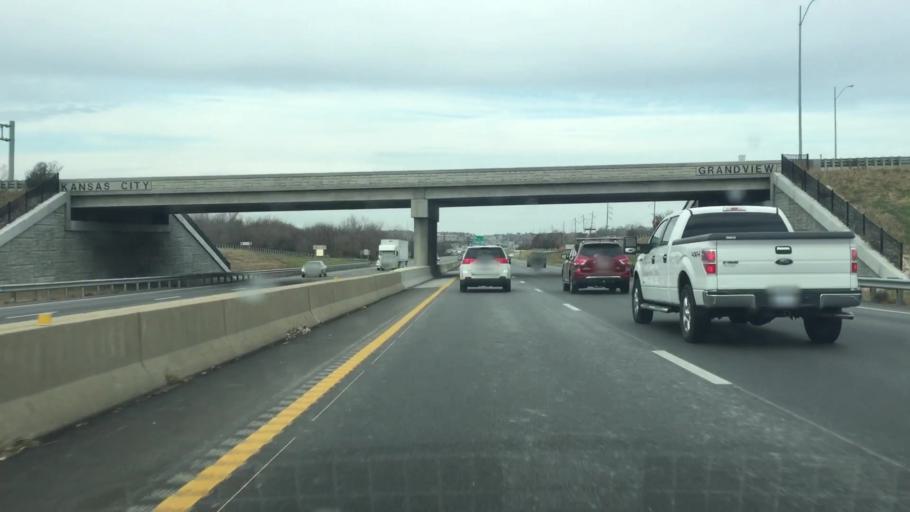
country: US
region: Missouri
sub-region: Cass County
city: Belton
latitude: 38.8430
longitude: -94.5295
